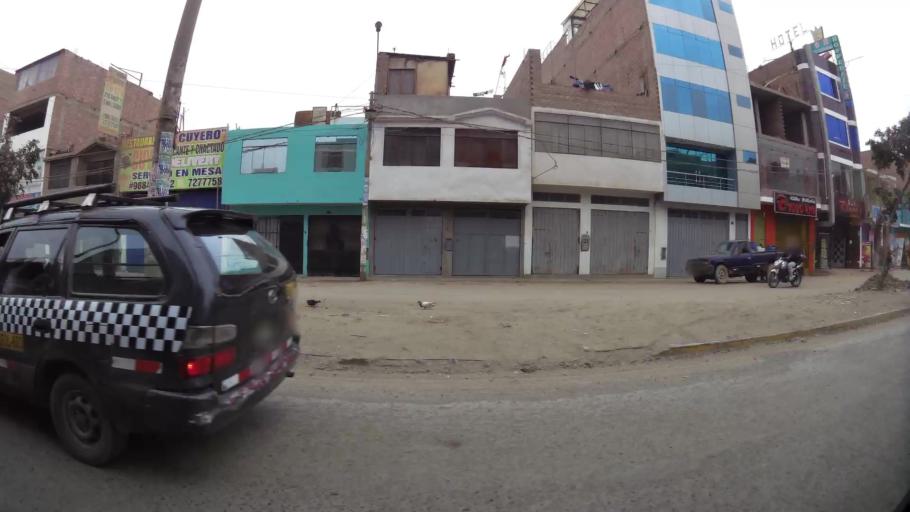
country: PE
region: Lima
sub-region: Lima
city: Independencia
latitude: -11.9662
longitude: -77.0907
